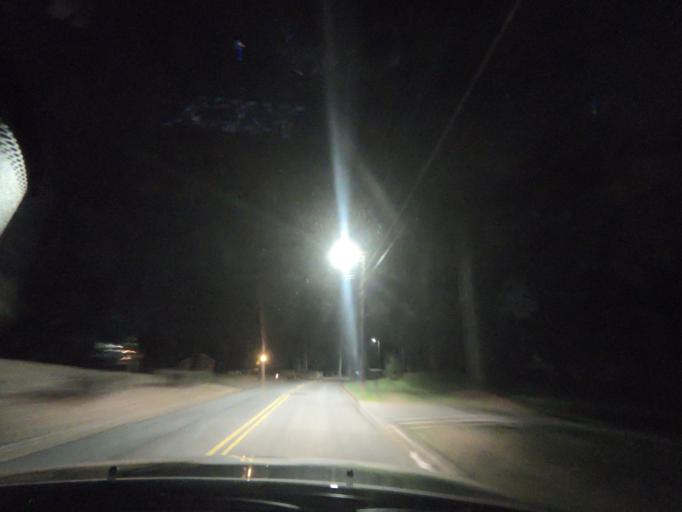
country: US
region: Georgia
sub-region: Fulton County
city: East Point
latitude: 33.6850
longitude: -84.4796
